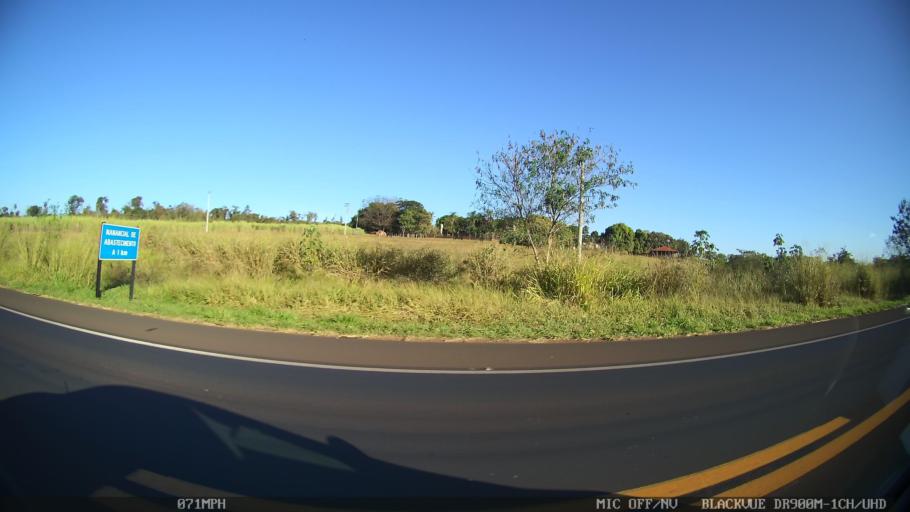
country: BR
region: Sao Paulo
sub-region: Guapiacu
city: Guapiacu
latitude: -20.7455
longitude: -49.1151
